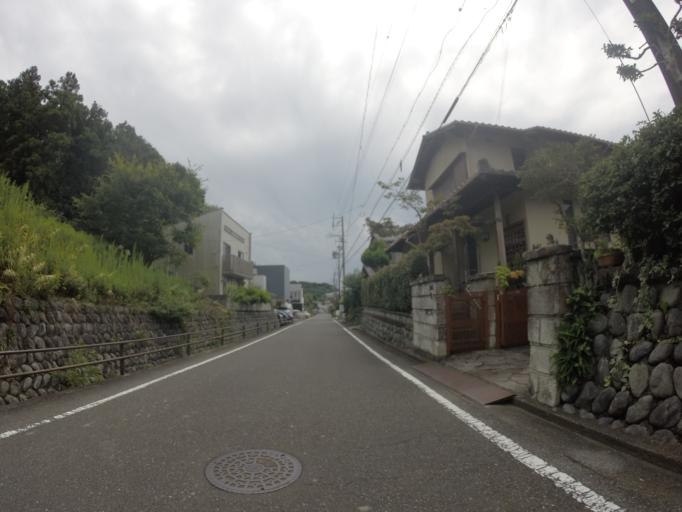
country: JP
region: Shizuoka
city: Shizuoka-shi
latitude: 34.9572
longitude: 138.4357
